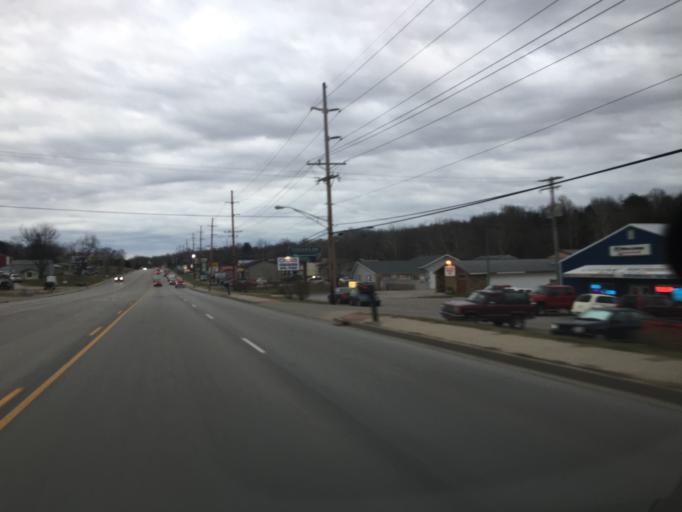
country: US
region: Indiana
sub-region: Monroe County
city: Ellettsville
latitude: 39.2213
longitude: -86.6061
